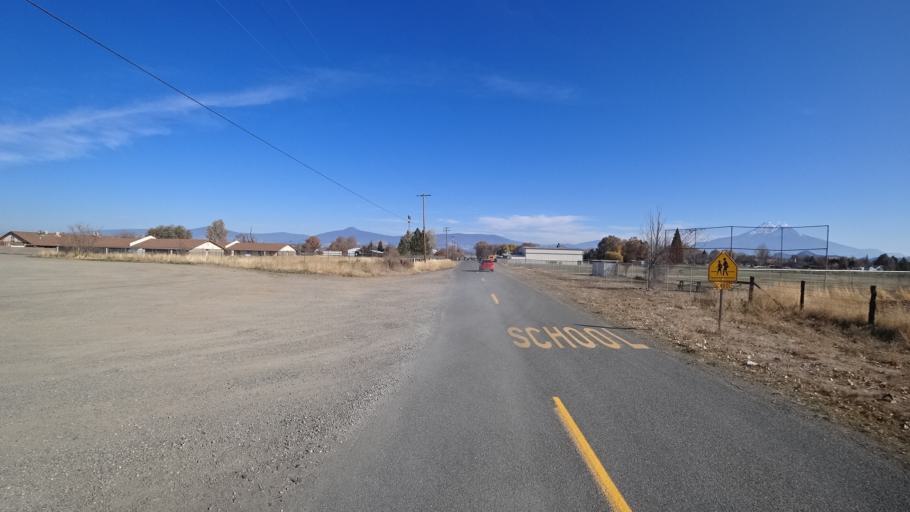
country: US
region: California
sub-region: Siskiyou County
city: Montague
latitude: 41.6457
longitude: -122.5280
